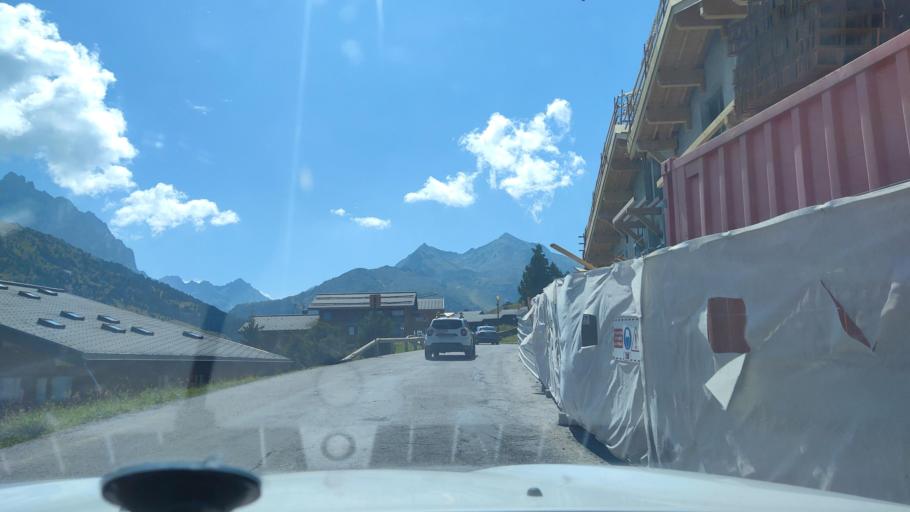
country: FR
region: Rhone-Alpes
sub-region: Departement de la Savoie
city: Meribel
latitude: 45.3738
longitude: 6.5745
